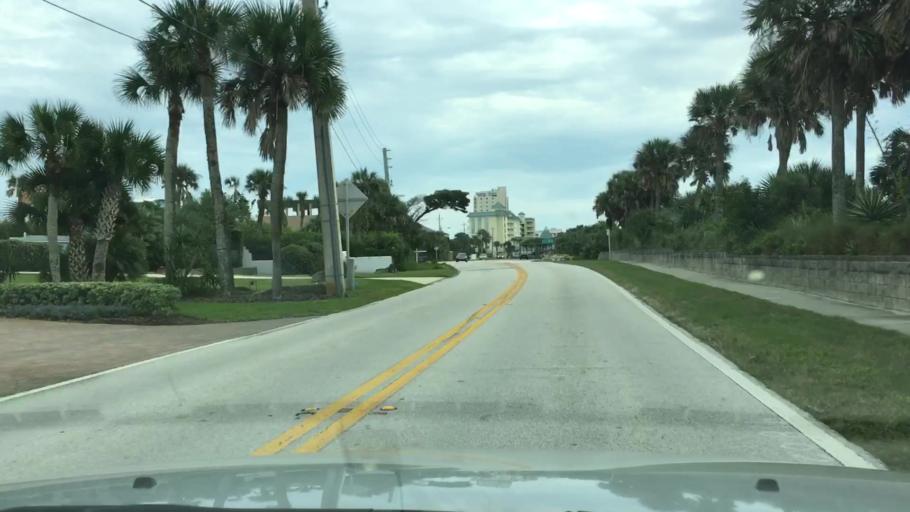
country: US
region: Florida
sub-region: Volusia County
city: Ormond Beach
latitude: 29.2950
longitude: -81.0414
